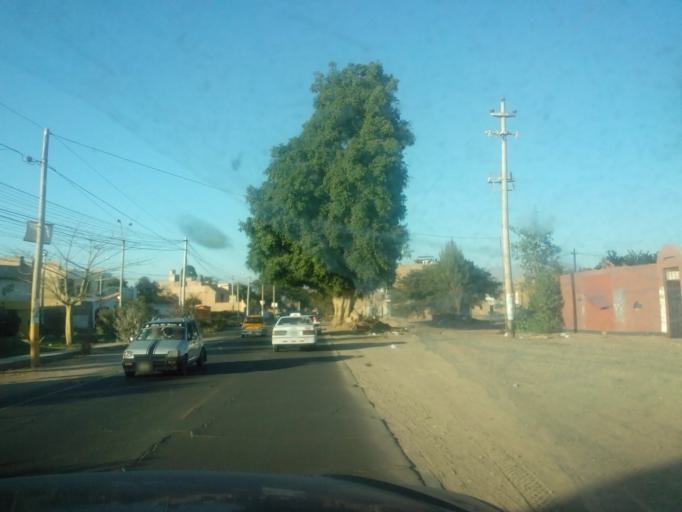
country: PE
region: Ica
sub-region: Provincia de Ica
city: Ica
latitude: -14.0789
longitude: -75.7462
